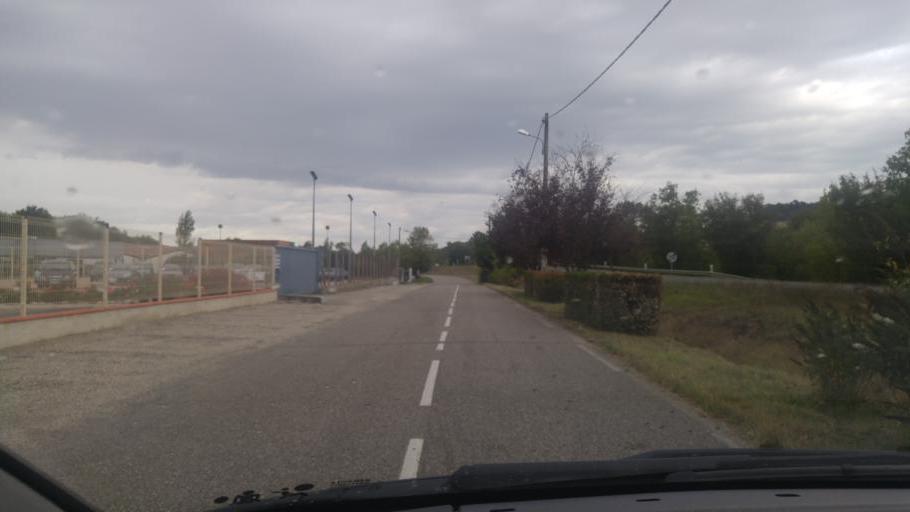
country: FR
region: Midi-Pyrenees
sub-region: Departement du Gers
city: Lectoure
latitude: 43.9142
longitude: 0.6302
